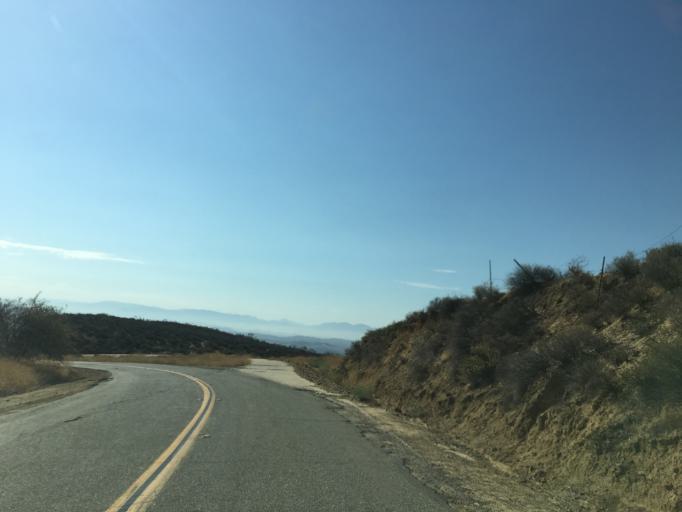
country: US
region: California
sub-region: Los Angeles County
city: Castaic
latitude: 34.5519
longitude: -118.6569
